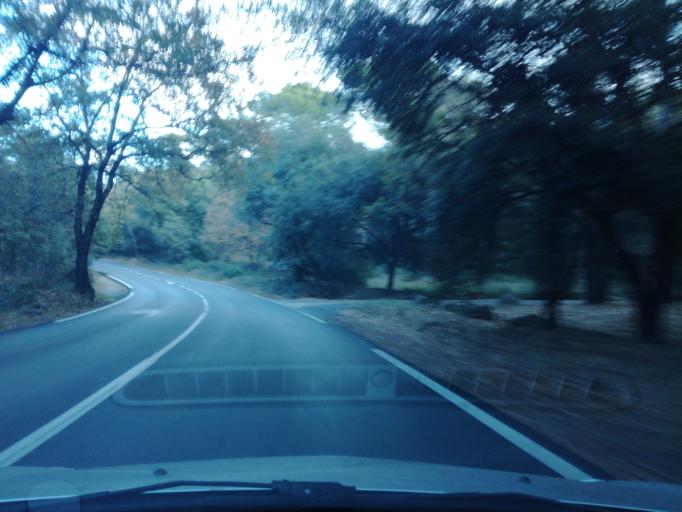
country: FR
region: Provence-Alpes-Cote d'Azur
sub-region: Departement des Alpes-Maritimes
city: Vallauris
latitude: 43.6030
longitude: 7.0408
